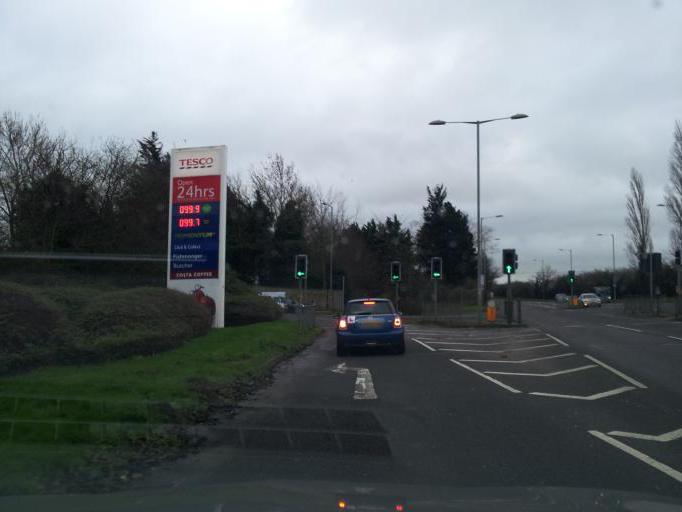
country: GB
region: England
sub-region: Norfolk
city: Cringleford
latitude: 52.5950
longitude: 1.2751
